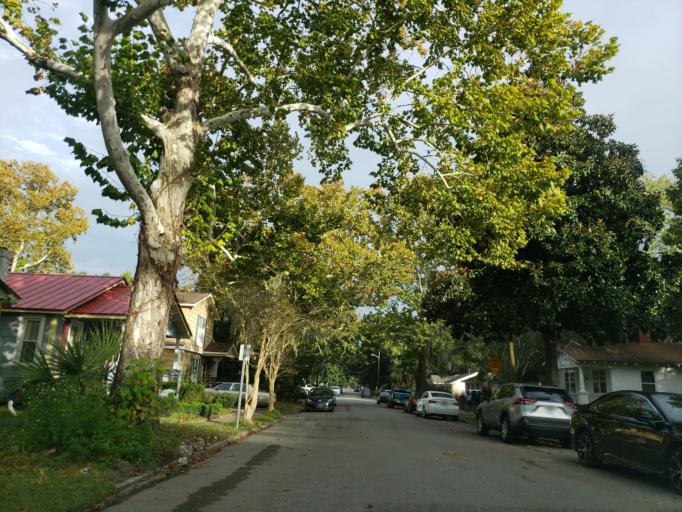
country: US
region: Georgia
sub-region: Chatham County
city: Savannah
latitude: 32.0596
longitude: -81.0771
